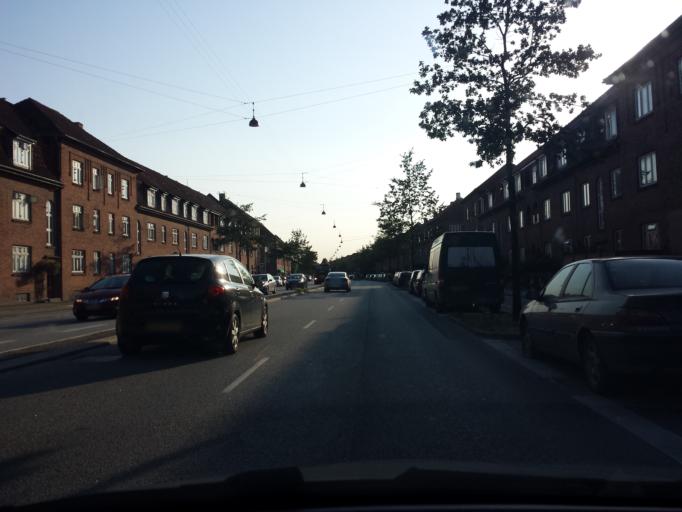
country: DK
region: Capital Region
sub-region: Frederiksberg Kommune
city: Frederiksberg
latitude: 55.6531
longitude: 12.5376
